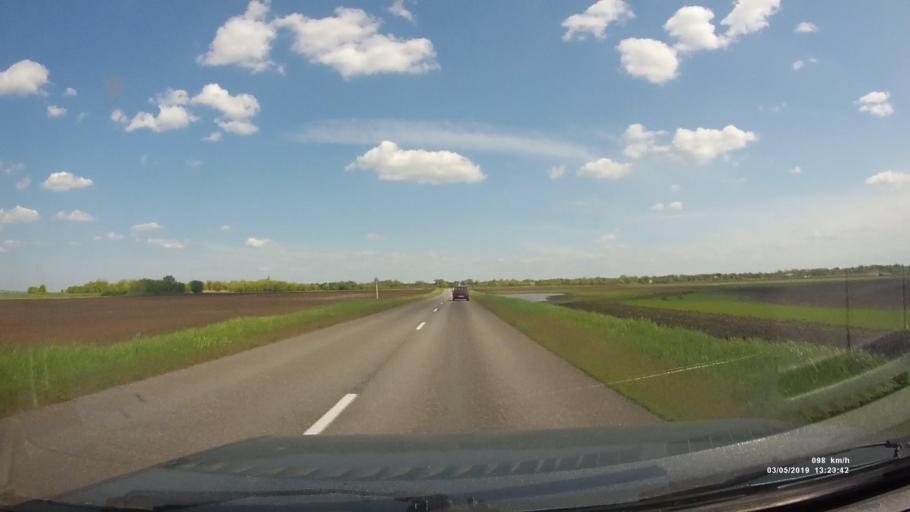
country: RU
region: Rostov
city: Semikarakorsk
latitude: 47.5626
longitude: 40.7879
